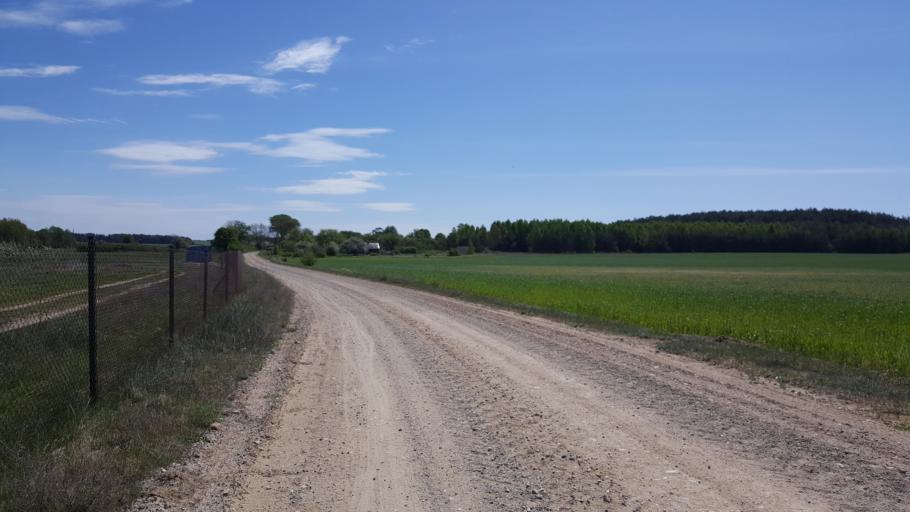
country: BY
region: Brest
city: Zhabinka
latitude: 52.3742
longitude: 24.0308
